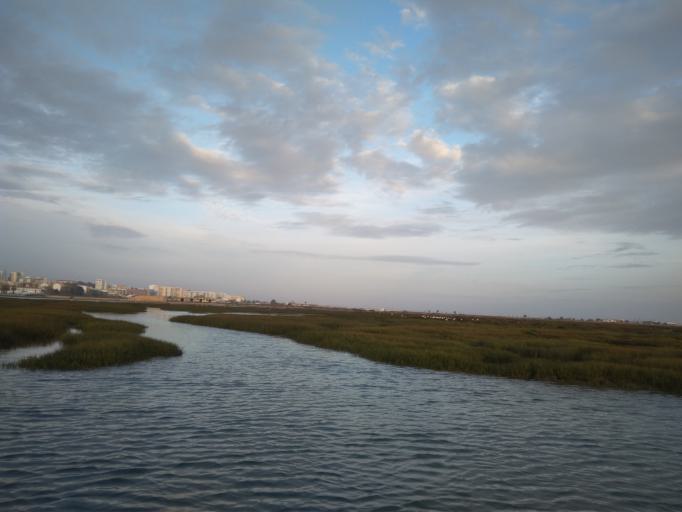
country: PT
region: Faro
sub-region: Faro
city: Faro
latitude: 37.0065
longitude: -7.9371
